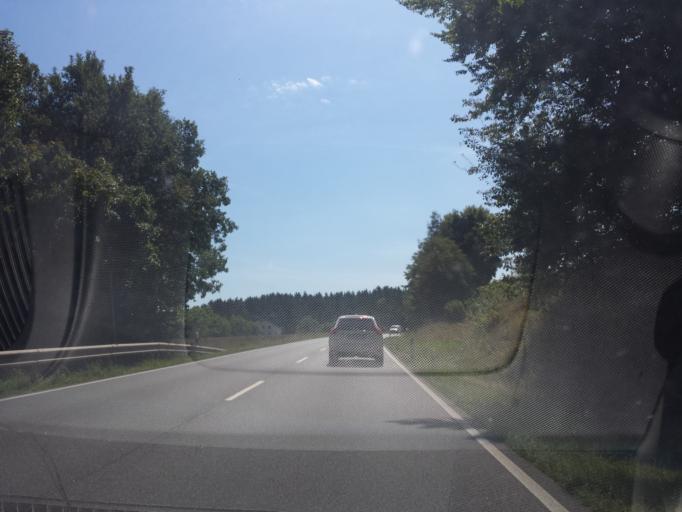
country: DE
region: Bavaria
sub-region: Lower Bavaria
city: Loitzendorf
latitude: 49.1150
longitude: 12.6506
